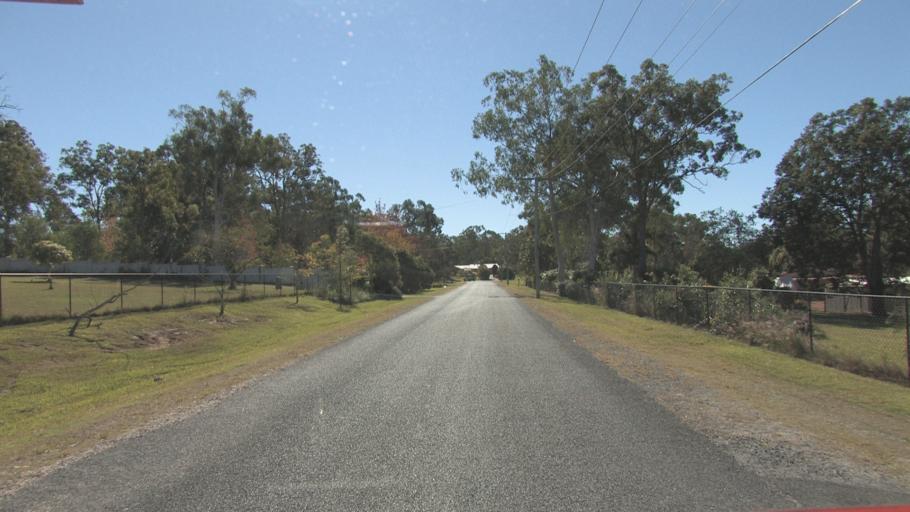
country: AU
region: Queensland
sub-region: Logan
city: Park Ridge South
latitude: -27.7110
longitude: 153.0414
